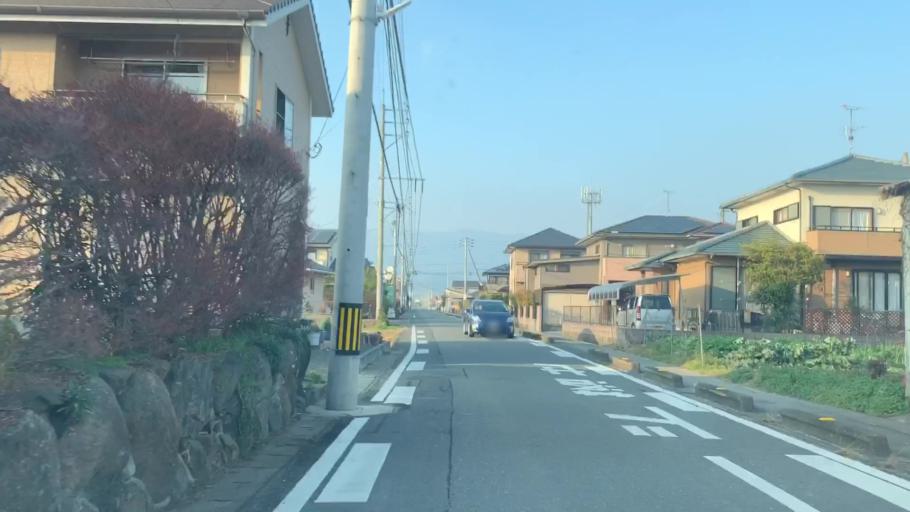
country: JP
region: Saga Prefecture
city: Saga-shi
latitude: 33.2711
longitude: 130.2292
